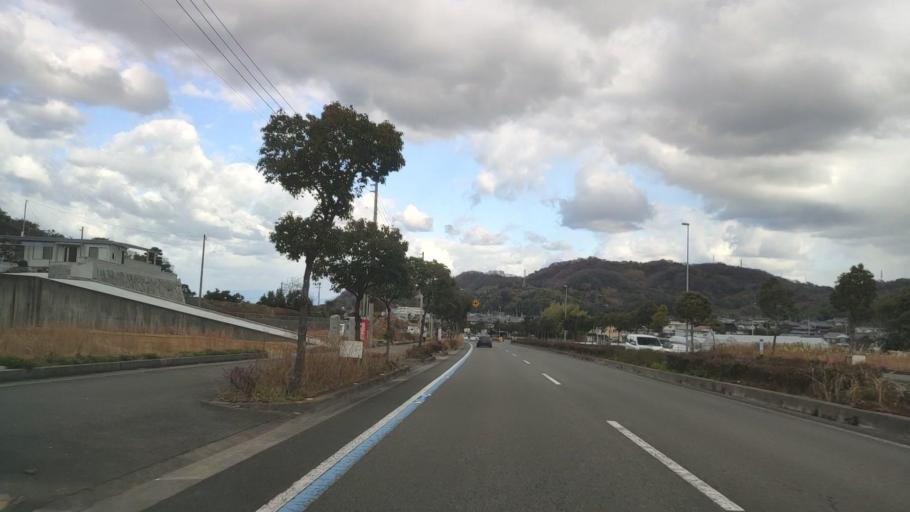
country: JP
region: Ehime
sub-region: Shikoku-chuo Shi
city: Matsuyama
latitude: 33.8941
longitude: 132.7580
